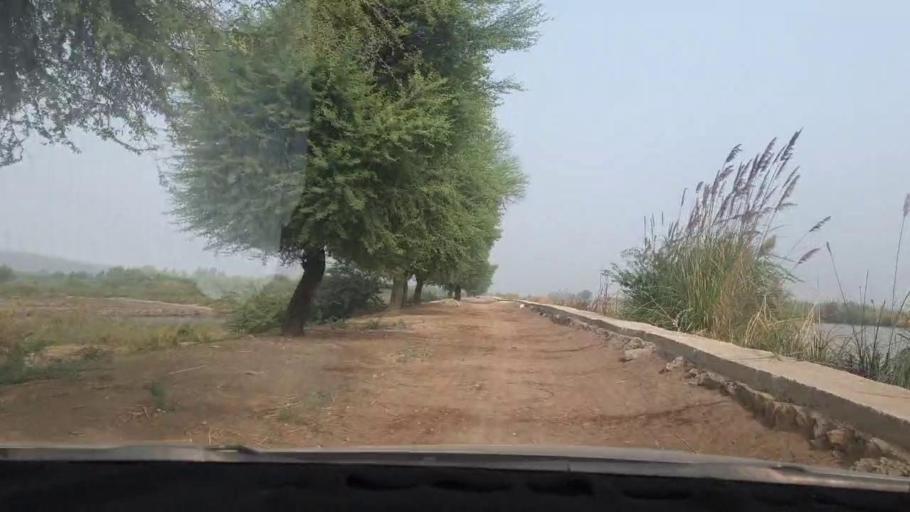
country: PK
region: Sindh
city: Matiari
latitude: 25.6653
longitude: 68.5593
